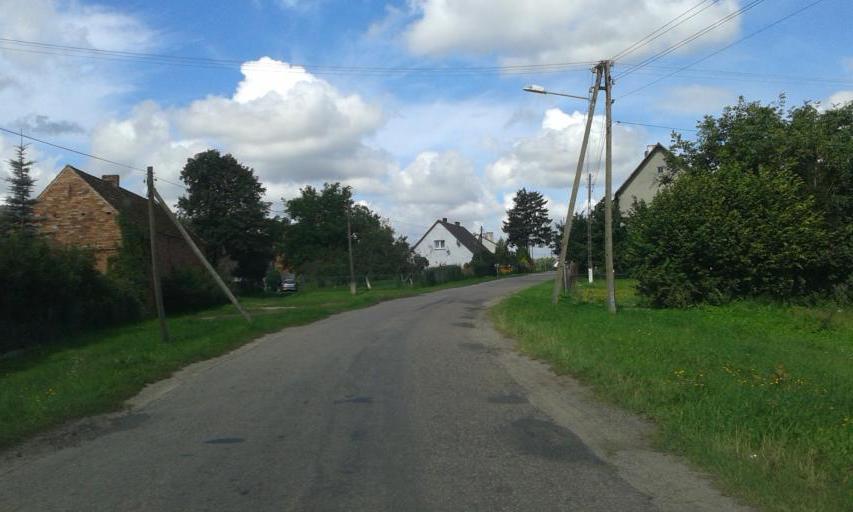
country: PL
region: West Pomeranian Voivodeship
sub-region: Powiat slawienski
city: Slawno
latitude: 54.3020
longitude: 16.6288
